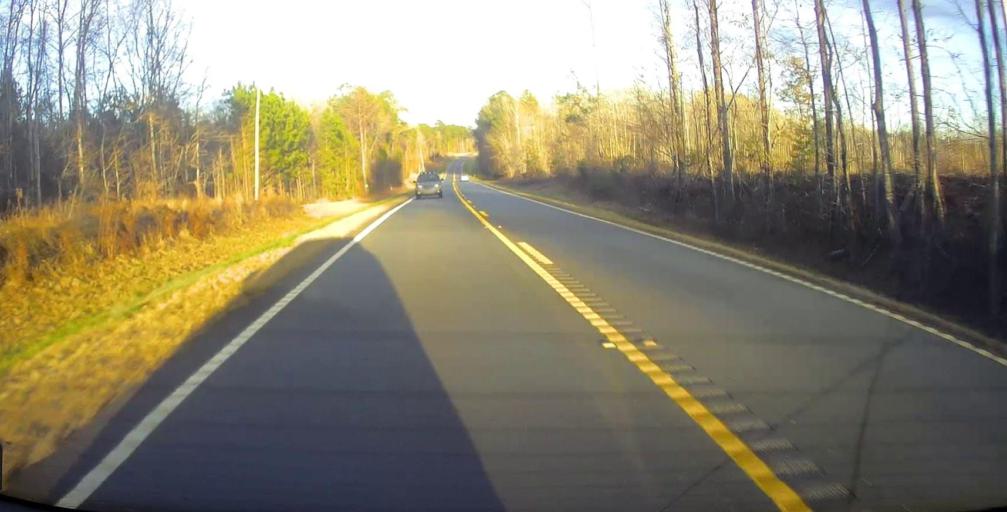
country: US
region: Georgia
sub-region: Talbot County
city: Sardis
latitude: 32.7191
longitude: -84.6745
